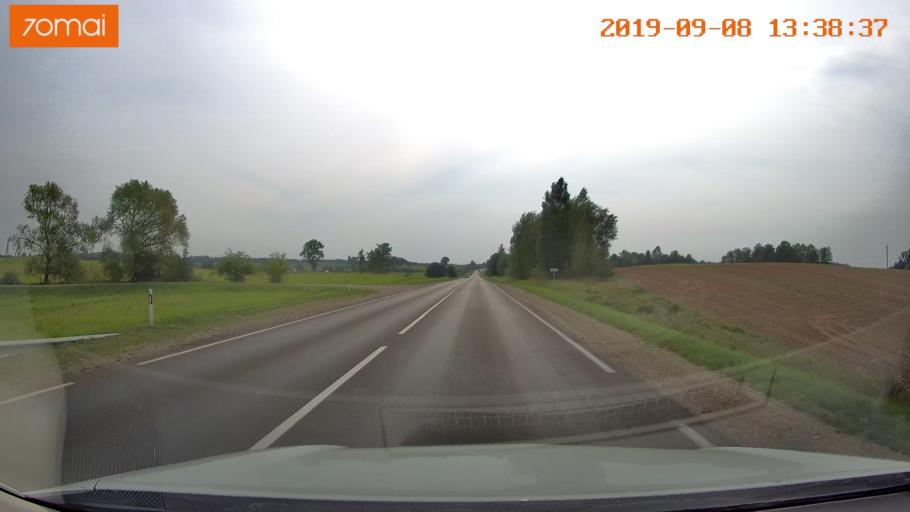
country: LT
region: Alytaus apskritis
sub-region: Alytus
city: Alytus
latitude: 54.4402
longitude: 24.1166
